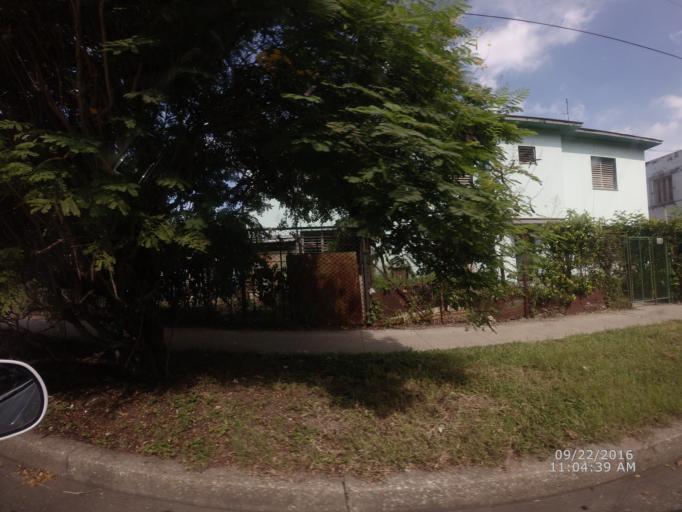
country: CU
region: La Habana
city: Havana
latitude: 23.1248
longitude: -82.4141
